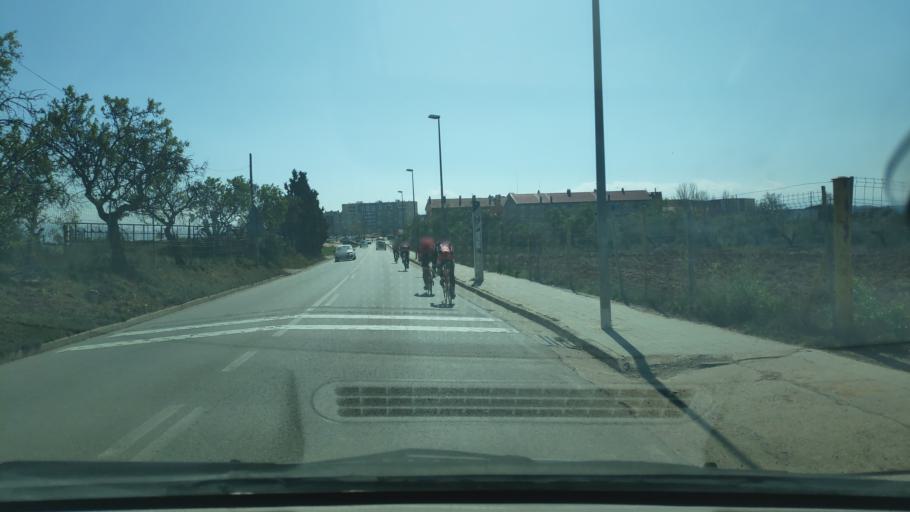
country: ES
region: Catalonia
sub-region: Provincia de Barcelona
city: Sabadell
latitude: 41.5541
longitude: 2.1261
